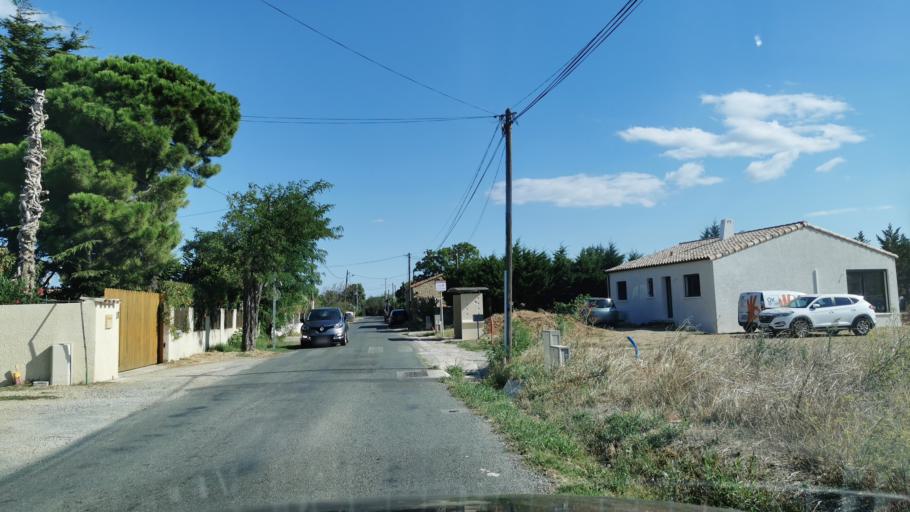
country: FR
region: Languedoc-Roussillon
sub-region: Departement de l'Aude
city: Ginestas
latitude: 43.2484
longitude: 2.8947
